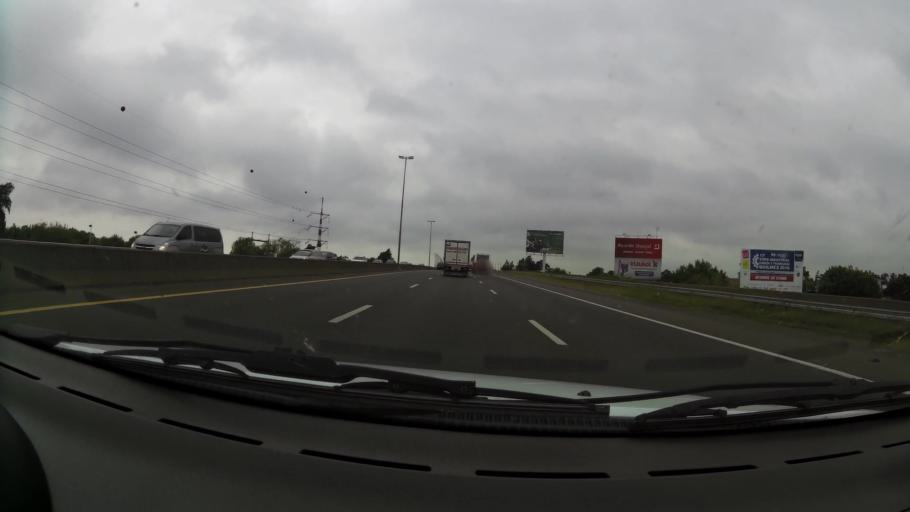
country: AR
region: Buenos Aires
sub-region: Partido de Quilmes
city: Quilmes
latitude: -34.7141
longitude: -58.2456
